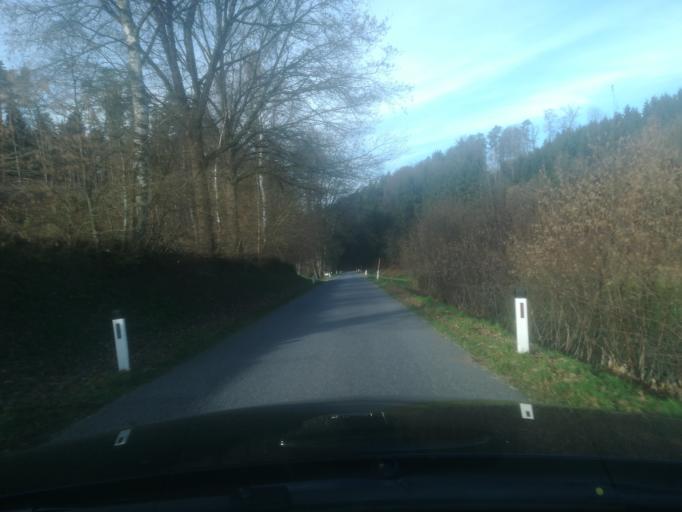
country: AT
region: Upper Austria
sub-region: Politischer Bezirk Perg
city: Perg
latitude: 48.3336
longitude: 14.6485
